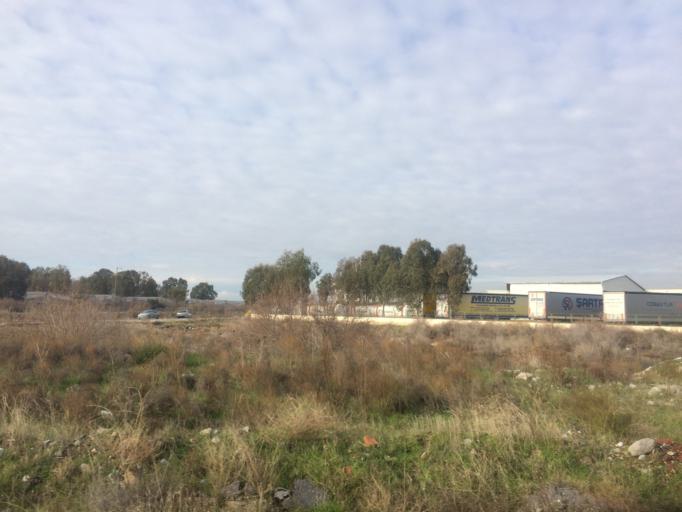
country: TR
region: Izmir
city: Menemen
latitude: 38.4945
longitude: 26.9440
